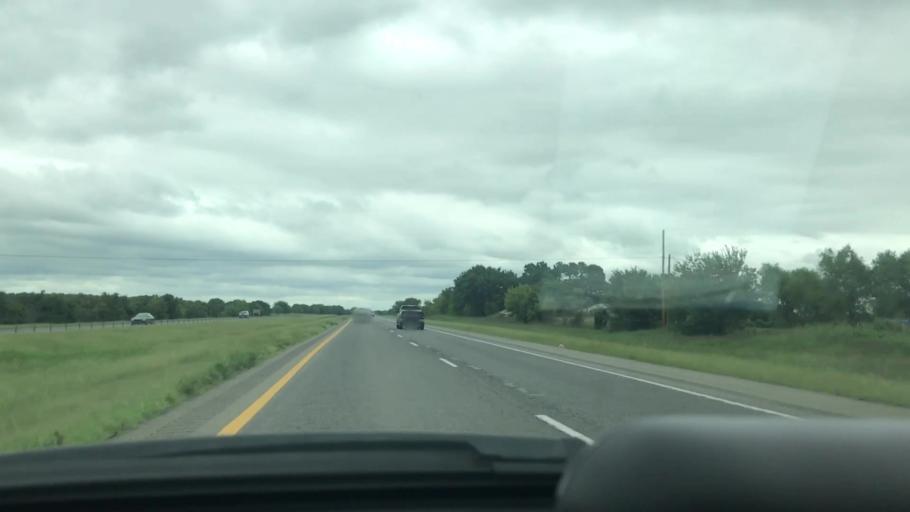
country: US
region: Oklahoma
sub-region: McIntosh County
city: Checotah
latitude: 35.4195
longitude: -95.5563
